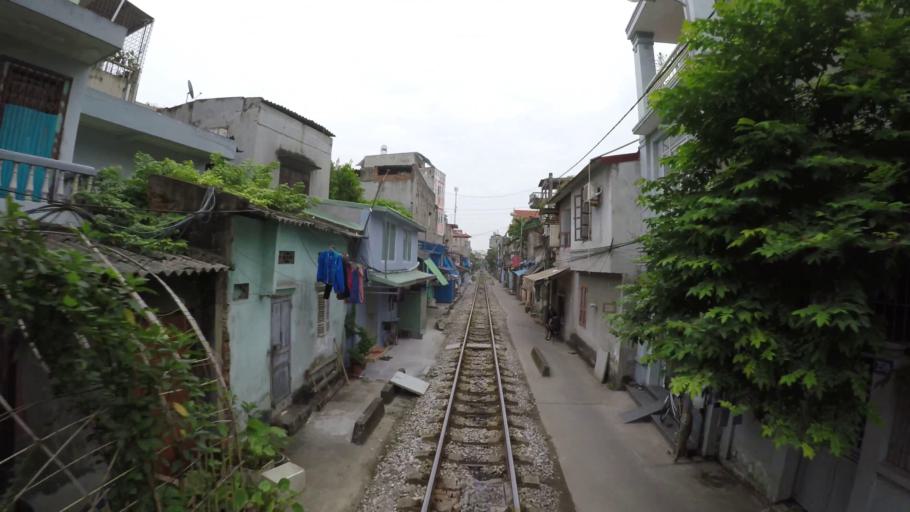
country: VN
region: Hai Phong
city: Haiphong
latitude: 20.8575
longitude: 106.6646
